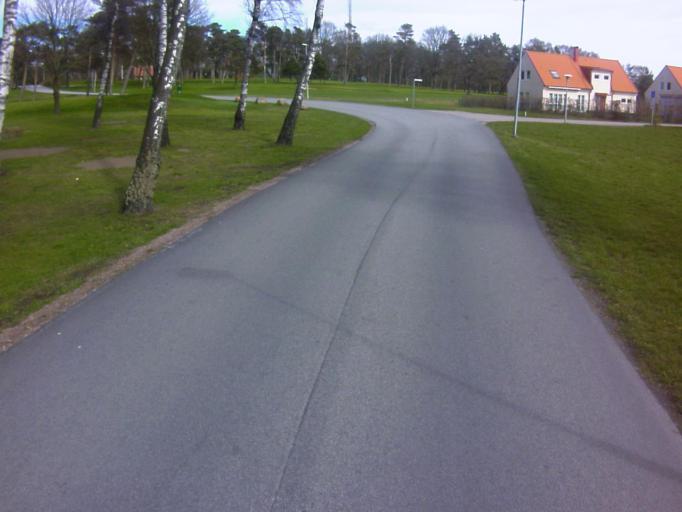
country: SE
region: Skane
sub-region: Kavlinge Kommun
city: Hofterup
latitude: 55.7881
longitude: 12.9466
